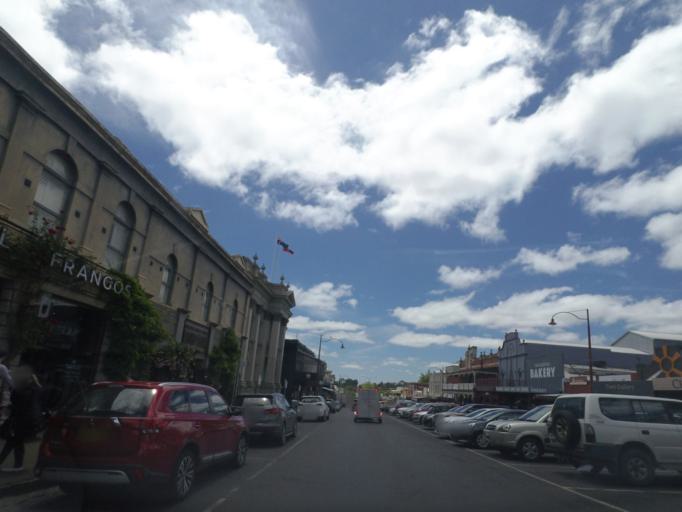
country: AU
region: Victoria
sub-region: Mount Alexander
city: Castlemaine
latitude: -37.3433
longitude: 144.1423
